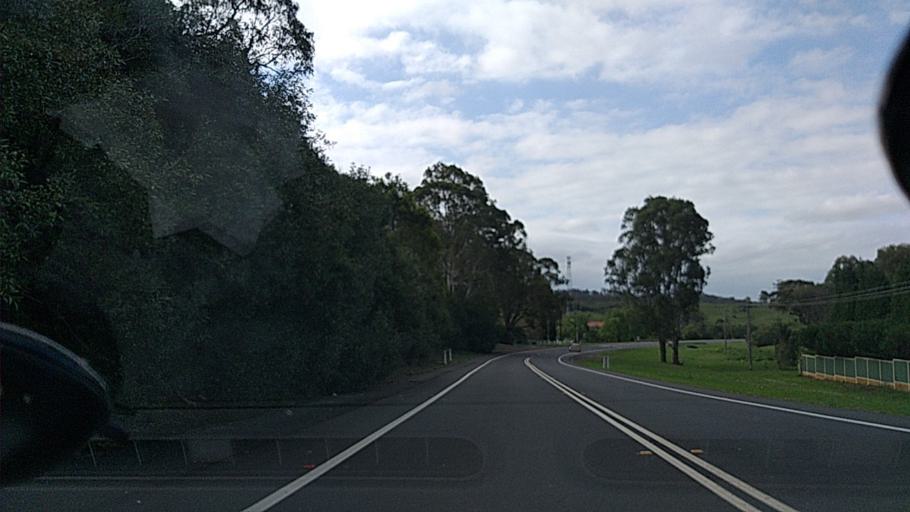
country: AU
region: New South Wales
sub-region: Campbelltown Municipality
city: Glen Alpine
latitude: -34.0875
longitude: 150.7740
